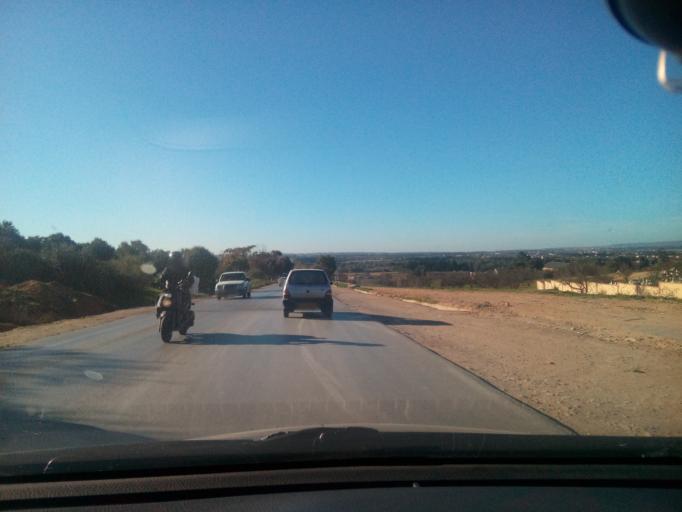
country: DZ
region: Mostaganem
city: Mostaganem
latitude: 35.8966
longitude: 0.2563
